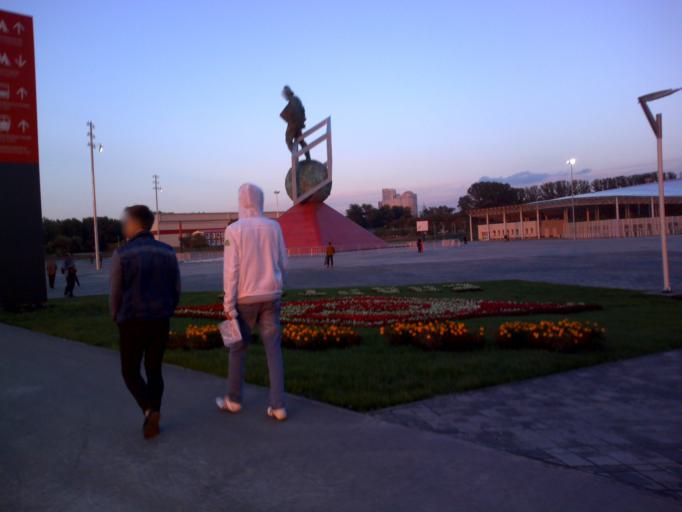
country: RU
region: Moscow
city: Shchukino
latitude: 55.8200
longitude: 37.4378
